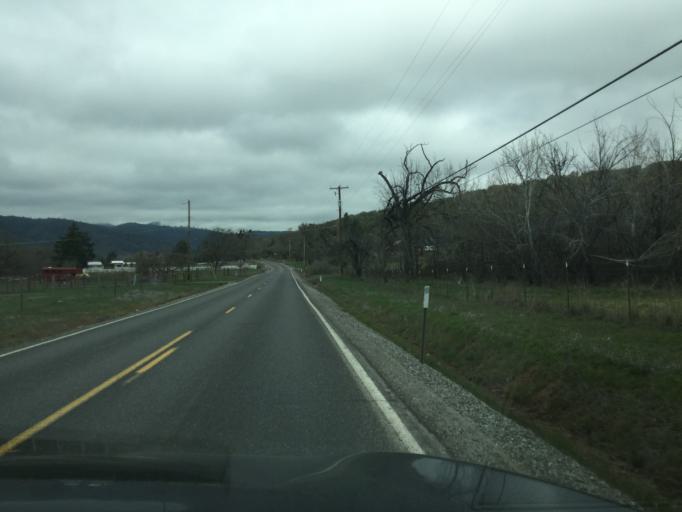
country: US
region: Oregon
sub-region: Jackson County
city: Gold Hill
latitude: 42.3938
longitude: -122.9968
